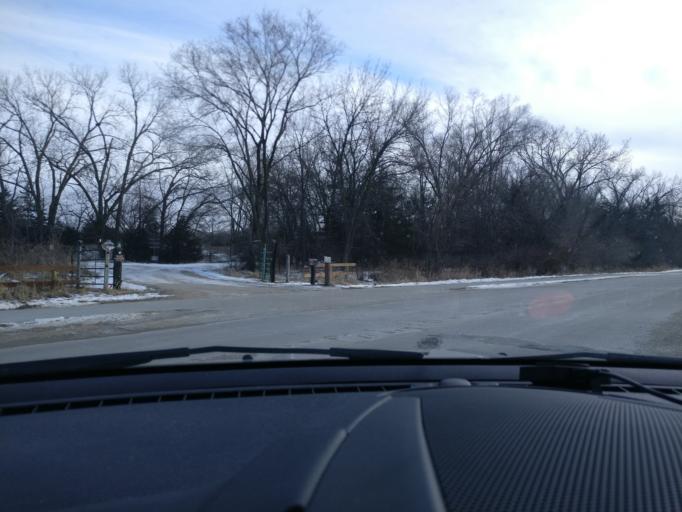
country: US
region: Nebraska
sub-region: Dodge County
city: Fremont
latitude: 41.4187
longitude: -96.5217
